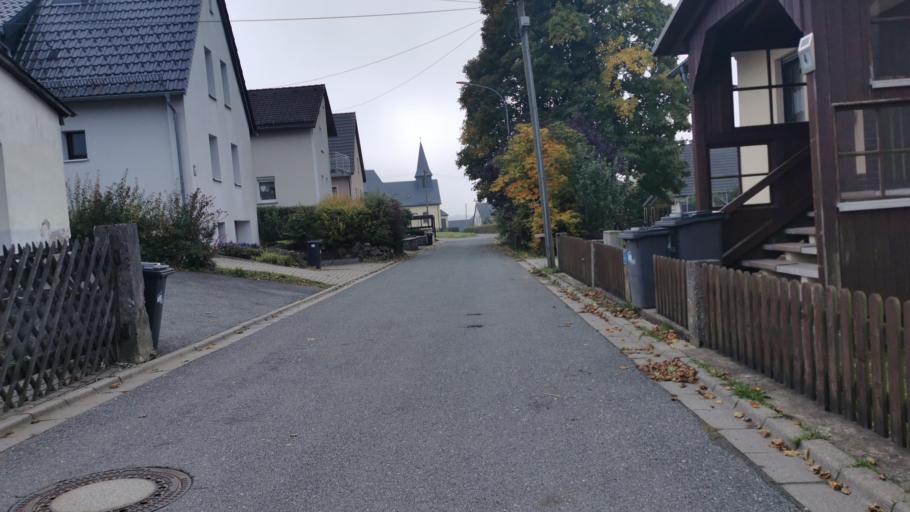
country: DE
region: Bavaria
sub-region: Upper Franconia
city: Tettau
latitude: 50.4447
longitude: 11.3165
